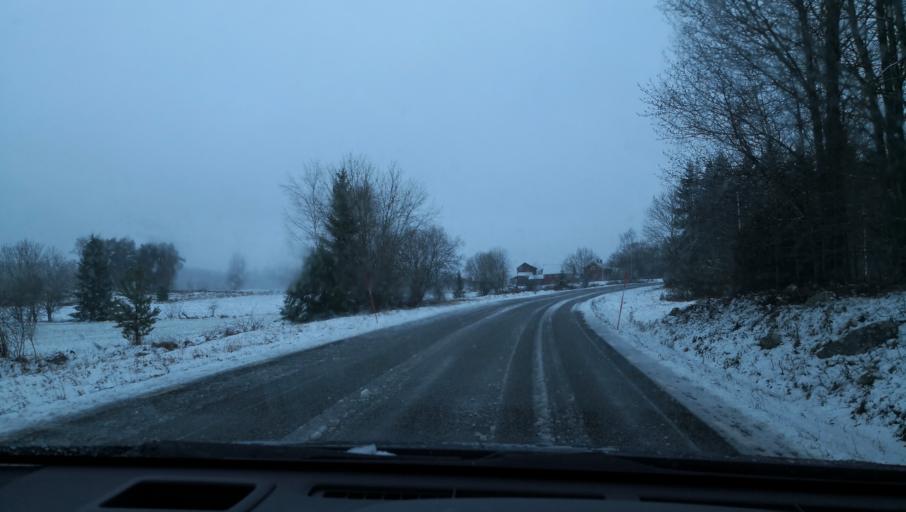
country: SE
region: Vaestmanland
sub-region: Kopings Kommun
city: Koping
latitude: 59.5770
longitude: 15.9668
